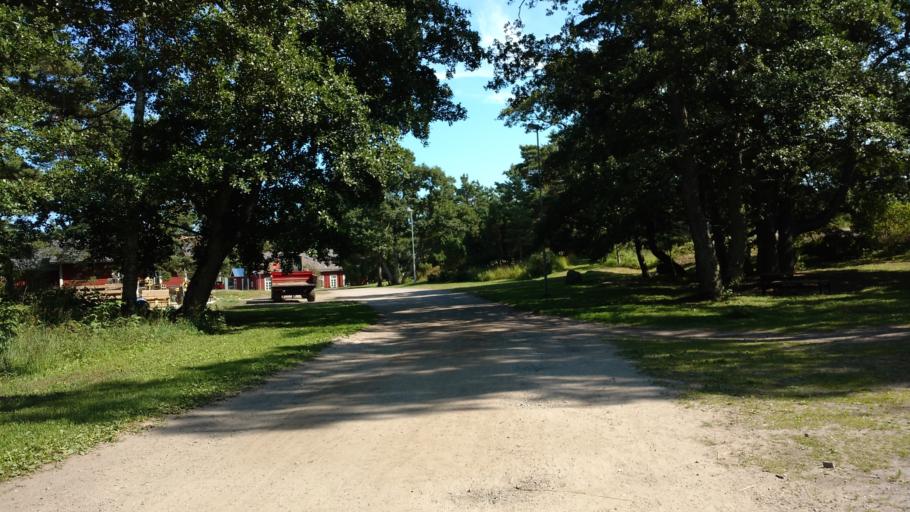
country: FI
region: Varsinais-Suomi
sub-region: Aboland-Turunmaa
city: Dragsfjaerd
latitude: 59.8073
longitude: 22.3335
